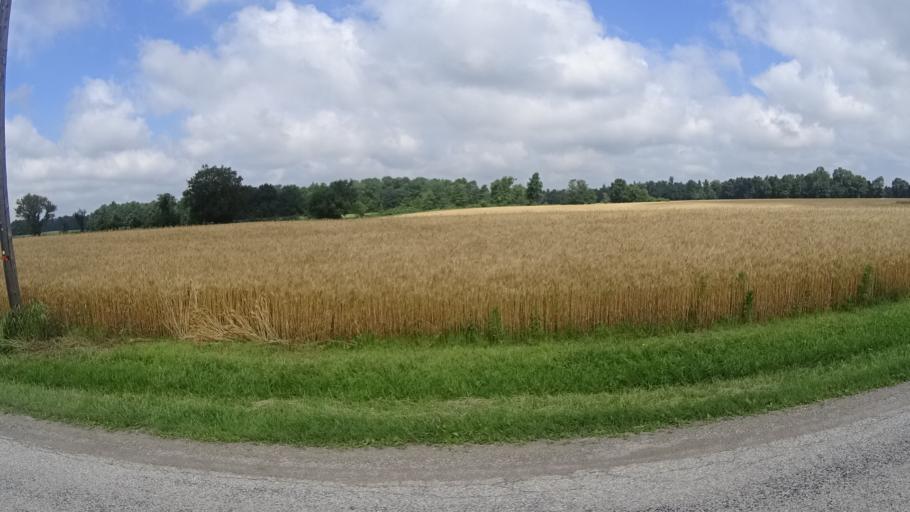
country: US
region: Ohio
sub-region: Huron County
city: Wakeman
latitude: 41.2944
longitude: -82.3905
